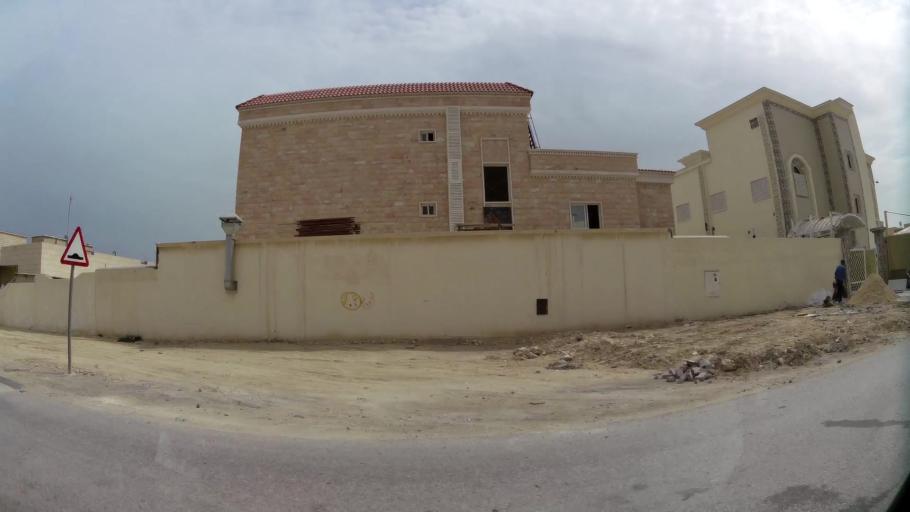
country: QA
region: Baladiyat ar Rayyan
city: Ar Rayyan
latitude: 25.3449
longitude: 51.4696
